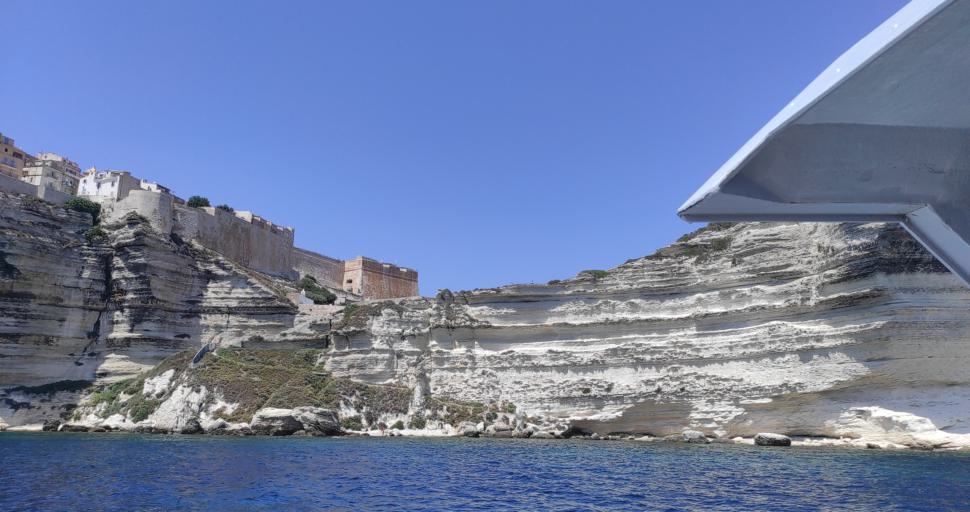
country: FR
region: Corsica
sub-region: Departement de la Corse-du-Sud
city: Bonifacio
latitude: 41.3851
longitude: 9.1611
